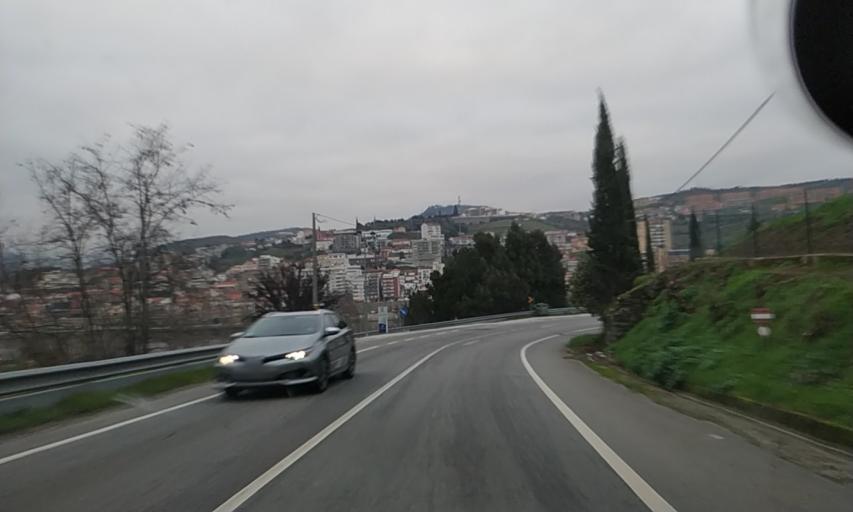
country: PT
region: Vila Real
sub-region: Peso da Regua
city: Peso da Regua
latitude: 41.1550
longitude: -7.7900
